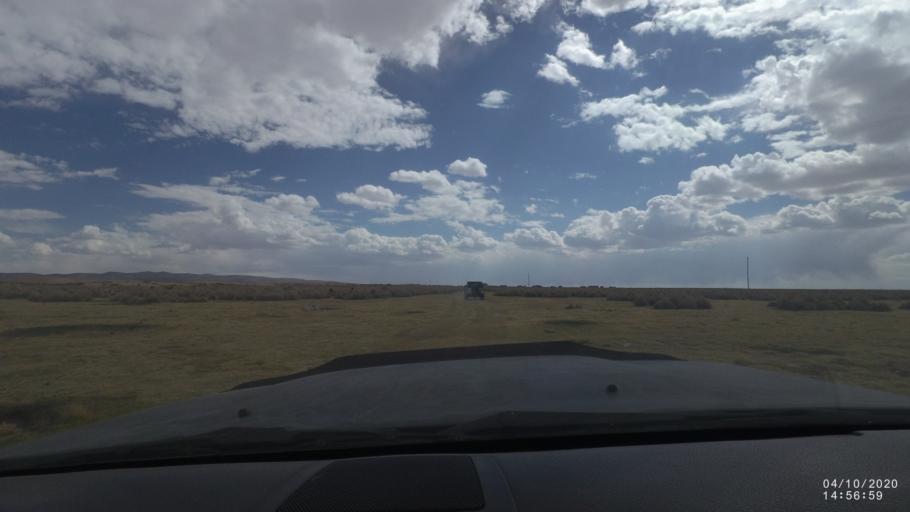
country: BO
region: Oruro
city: Poopo
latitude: -18.6850
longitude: -67.5175
